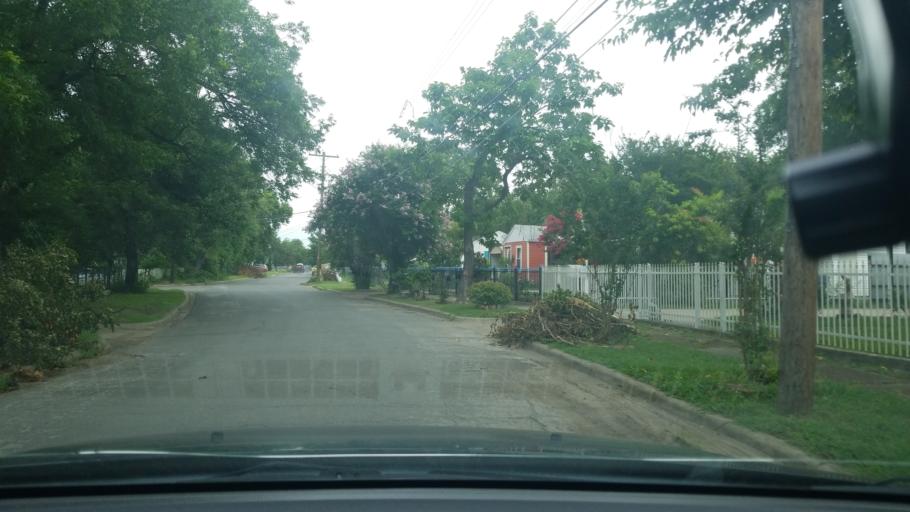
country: US
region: Texas
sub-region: Dallas County
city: Balch Springs
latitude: 32.7725
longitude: -96.6897
